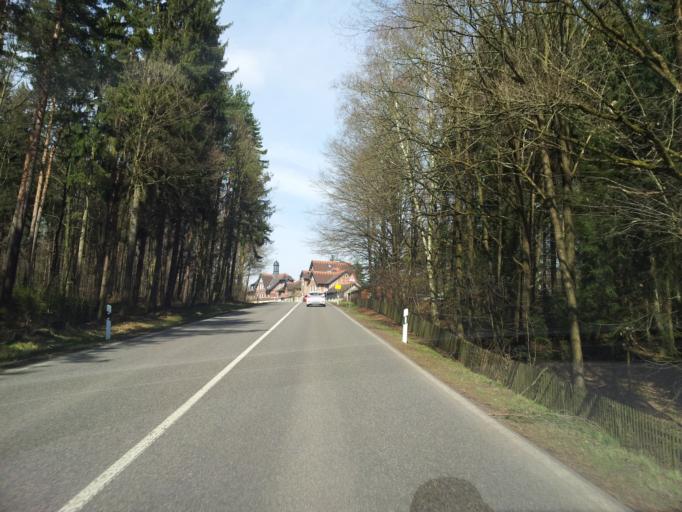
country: DE
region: Saxony
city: Bernsdorf
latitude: 50.8026
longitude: 12.6720
